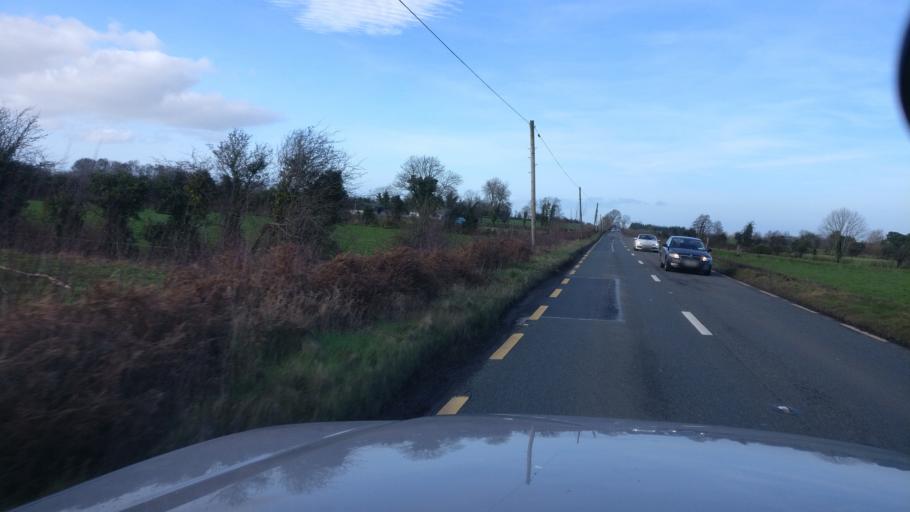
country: IE
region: Leinster
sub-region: Laois
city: Mountmellick
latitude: 53.0923
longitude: -7.3358
